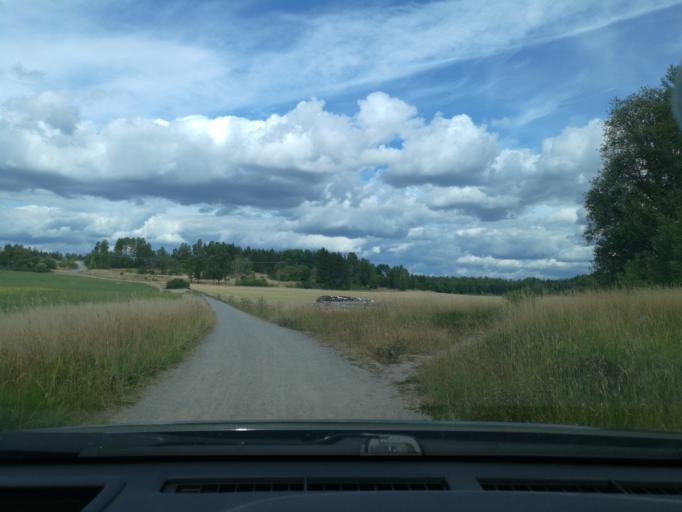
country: SE
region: Stockholm
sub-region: Sigtuna Kommun
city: Marsta
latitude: 59.6158
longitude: 17.8017
